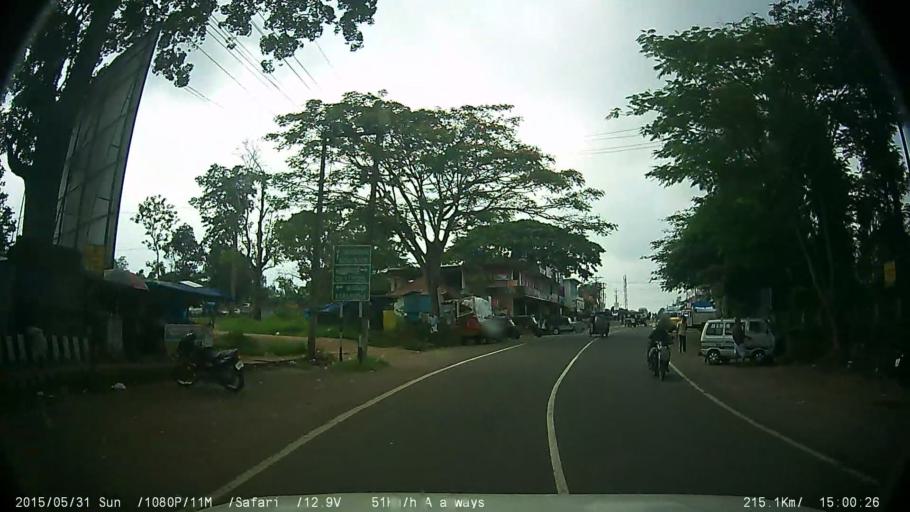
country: IN
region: Kerala
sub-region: Wayanad
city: Kalpetta
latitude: 11.6170
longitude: 76.2111
